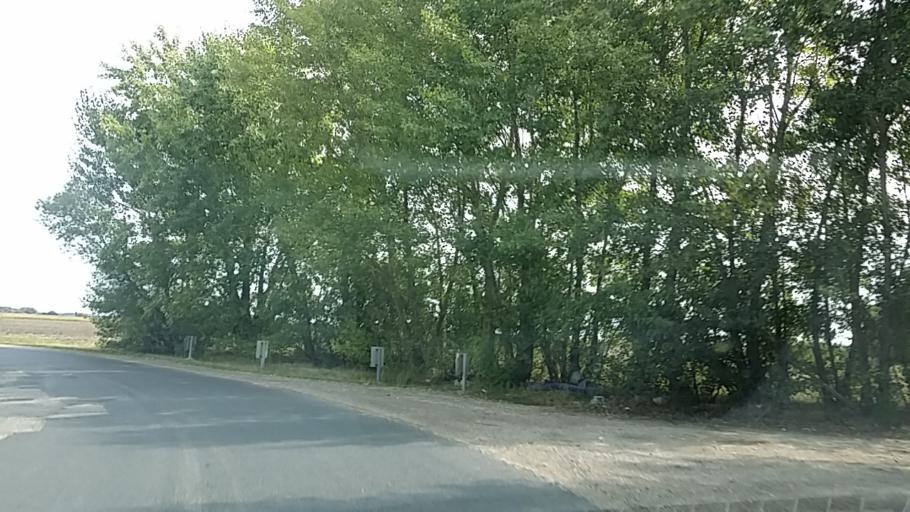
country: HU
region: Gyor-Moson-Sopron
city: Bosarkany
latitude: 47.6952
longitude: 17.2659
